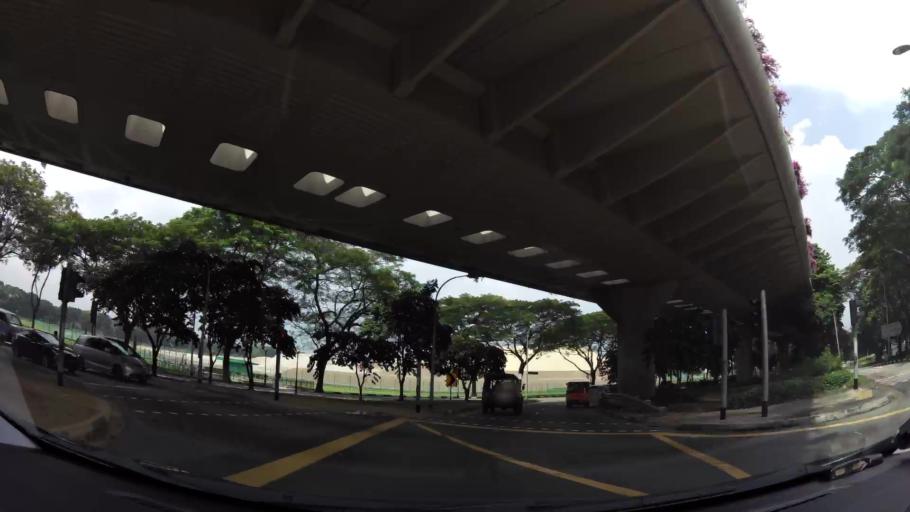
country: SG
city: Singapore
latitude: 1.3451
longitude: 103.9186
